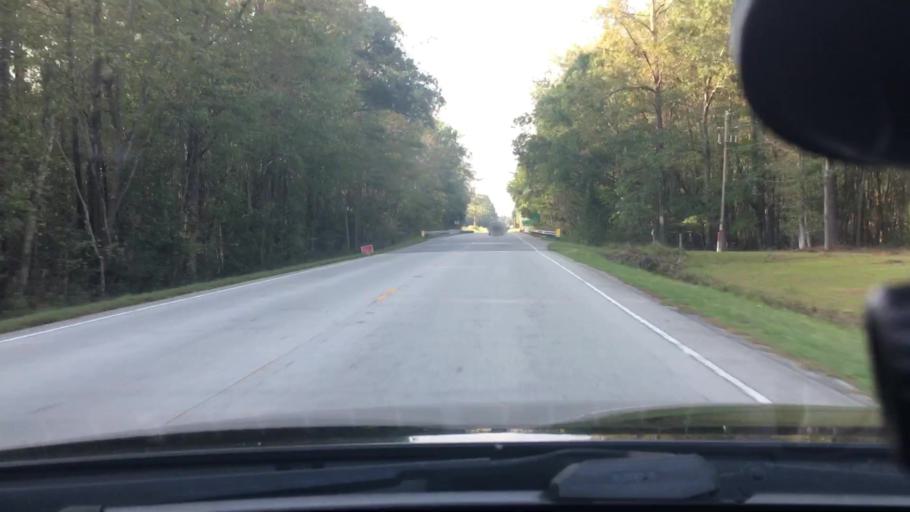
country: US
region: North Carolina
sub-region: Craven County
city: Vanceboro
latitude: 35.3906
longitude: -77.2306
